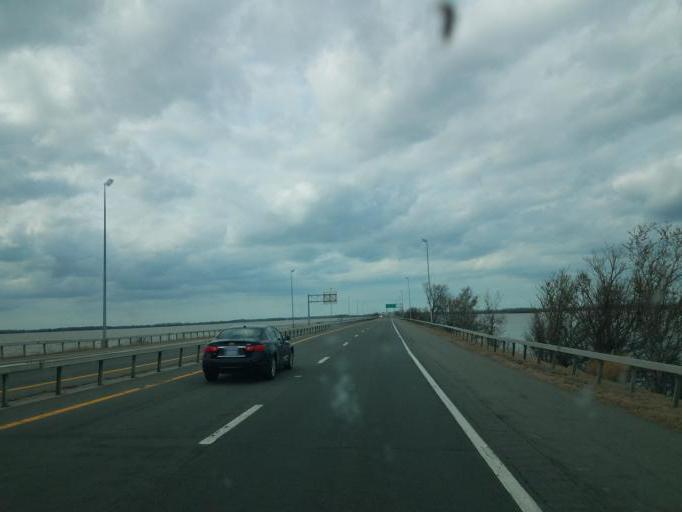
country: US
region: Ohio
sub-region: Ottawa County
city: Port Clinton
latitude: 41.4679
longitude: -82.8327
